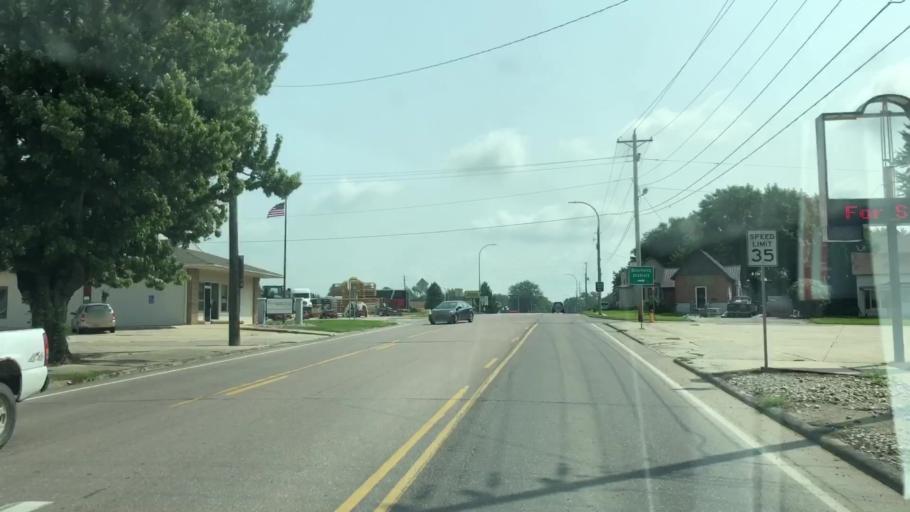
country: US
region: Iowa
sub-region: O'Brien County
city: Sheldon
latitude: 43.1858
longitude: -95.8536
